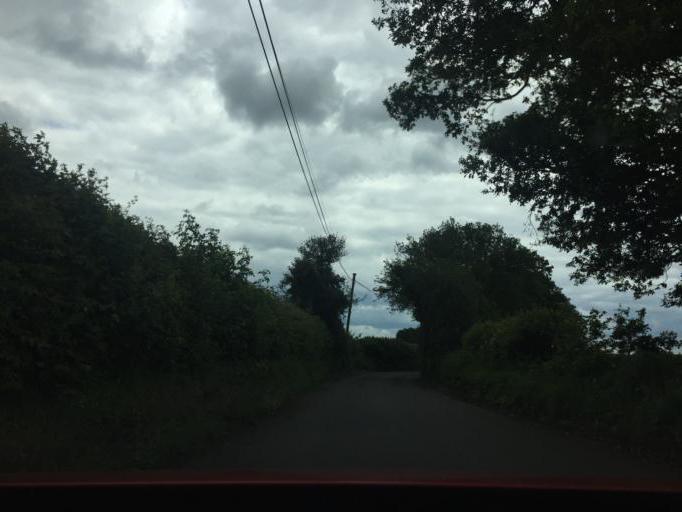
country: GB
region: England
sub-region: Hertfordshire
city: Wheathampstead
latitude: 51.8530
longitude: -0.3192
